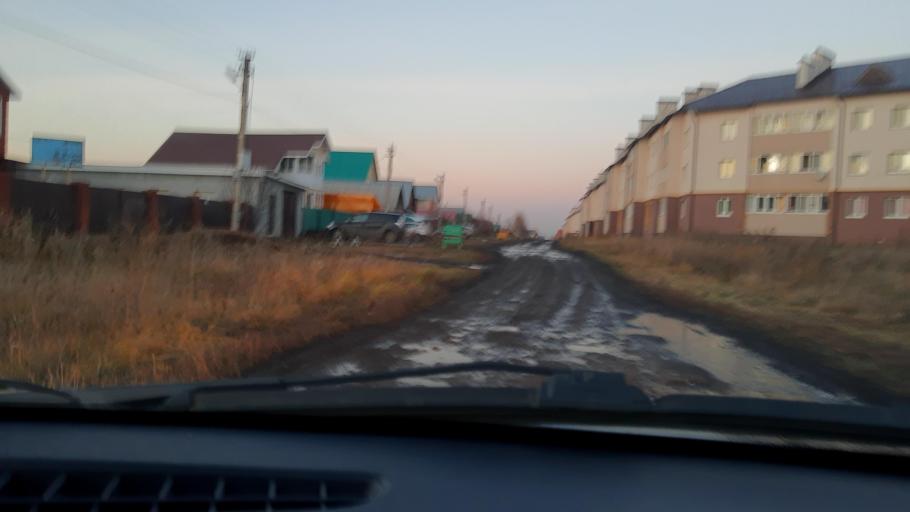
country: RU
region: Bashkortostan
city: Avdon
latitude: 54.6953
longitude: 55.8018
